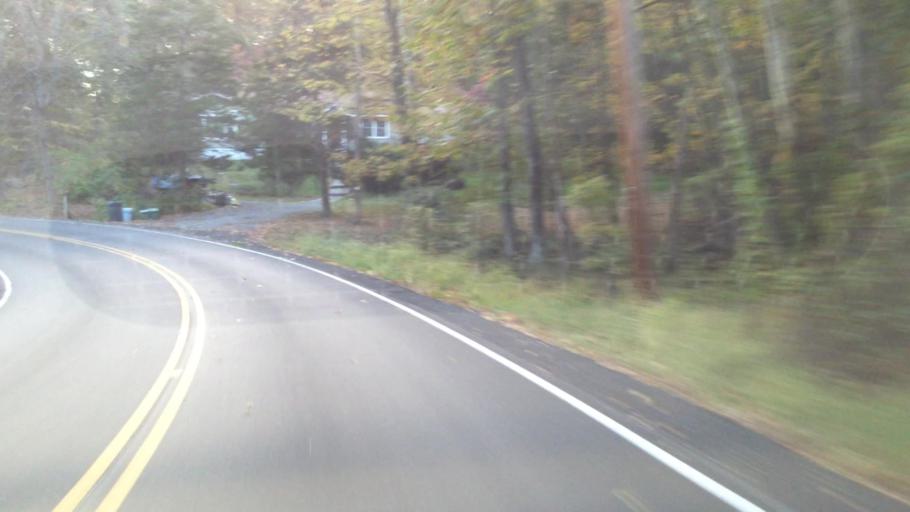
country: US
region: New York
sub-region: Ulster County
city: Tillson
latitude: 41.8257
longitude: -74.0054
